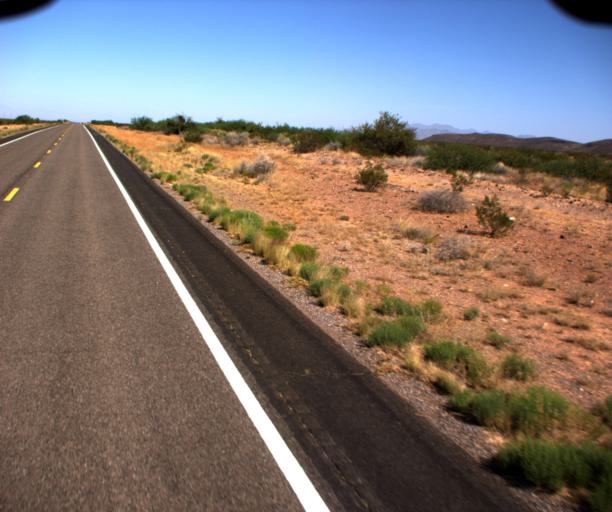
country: US
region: Arizona
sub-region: Graham County
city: Swift Trail Junction
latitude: 32.7563
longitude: -109.4255
